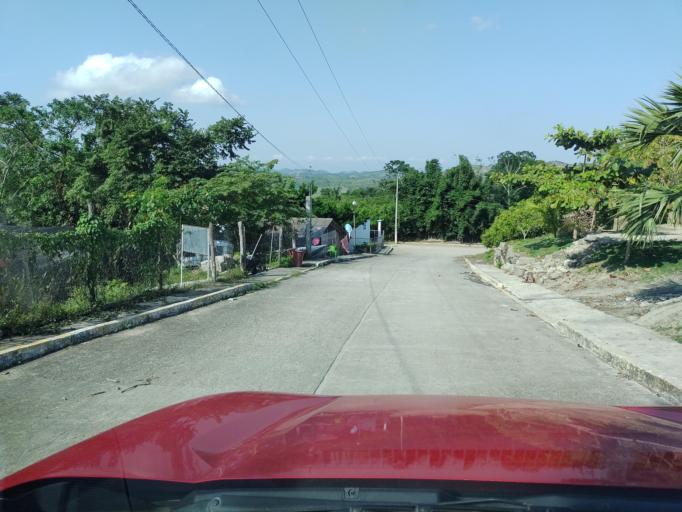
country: MX
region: Veracruz
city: Agua Dulce
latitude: 20.2877
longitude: -97.1846
